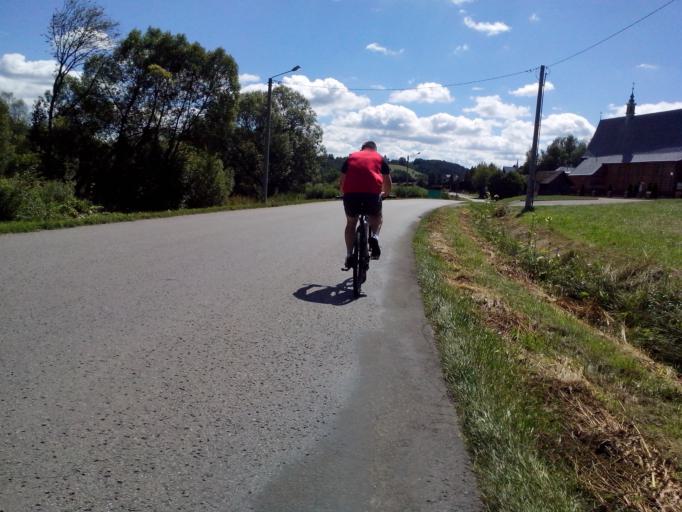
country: PL
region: Subcarpathian Voivodeship
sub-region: Powiat brzozowski
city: Golcowa
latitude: 49.7778
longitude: 21.9976
